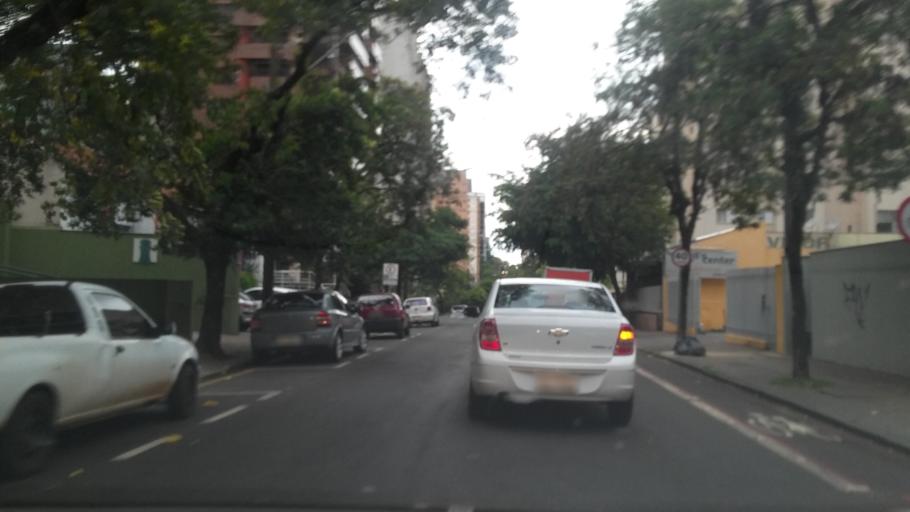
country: BR
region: Parana
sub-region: Londrina
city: Londrina
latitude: -23.3177
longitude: -51.1646
